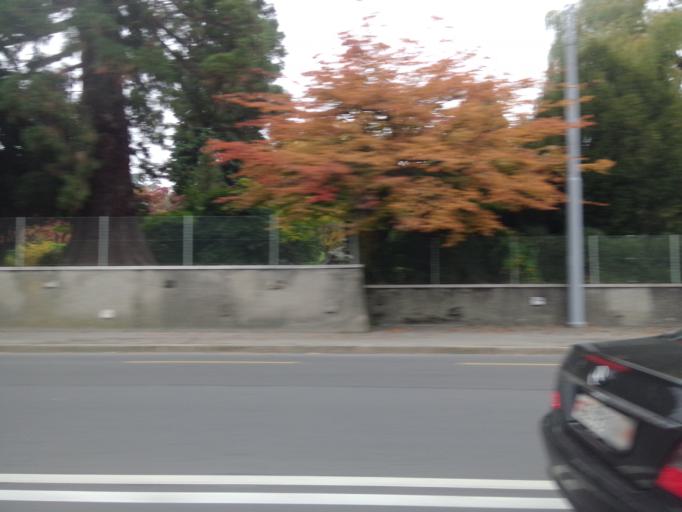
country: CH
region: Geneva
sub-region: Geneva
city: Les Avanchets
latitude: 46.2105
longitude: 6.1162
